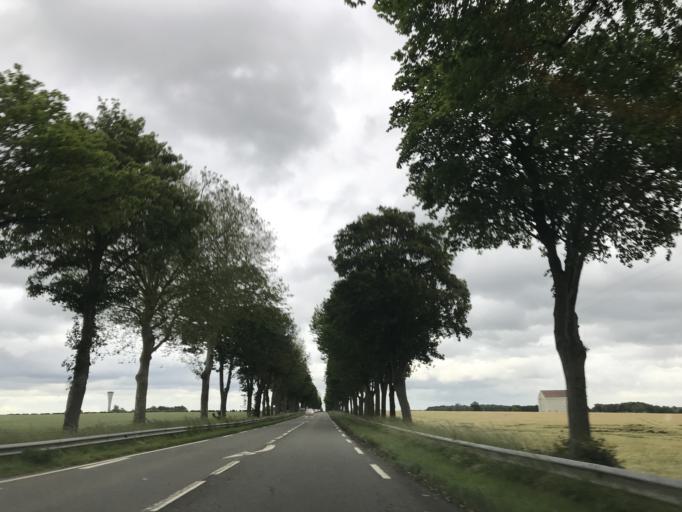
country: FR
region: Ile-de-France
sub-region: Departement des Yvelines
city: Bennecourt
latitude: 49.0230
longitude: 1.5089
